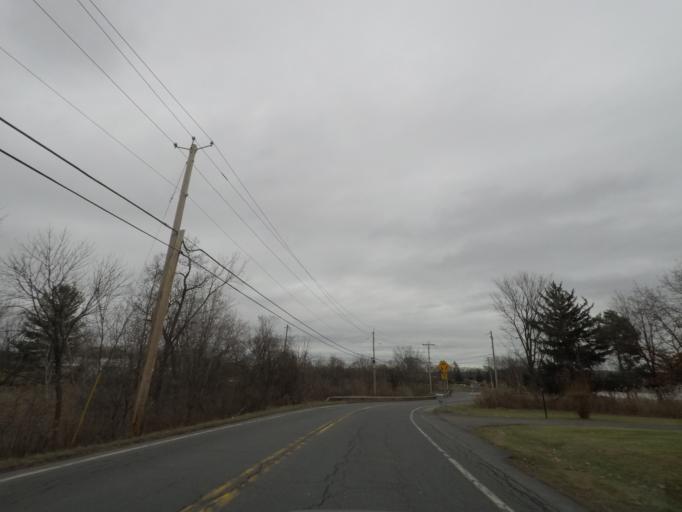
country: US
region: New York
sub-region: Albany County
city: Cohoes
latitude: 42.7652
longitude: -73.7335
